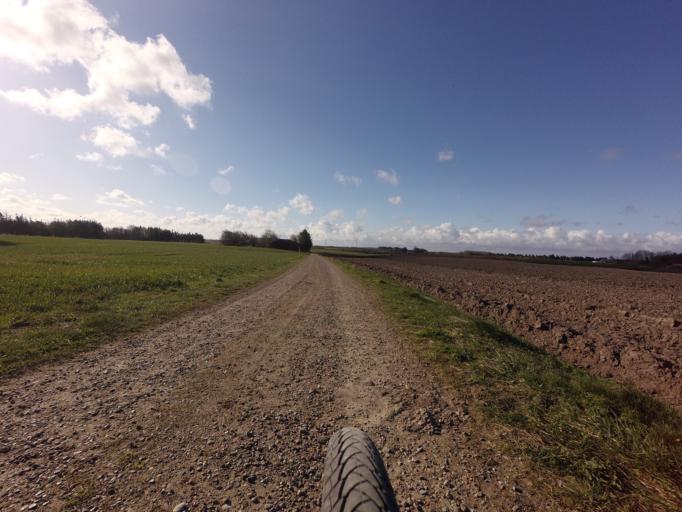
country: DK
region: North Denmark
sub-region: Hjorring Kommune
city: Vra
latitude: 57.3624
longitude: 9.8167
